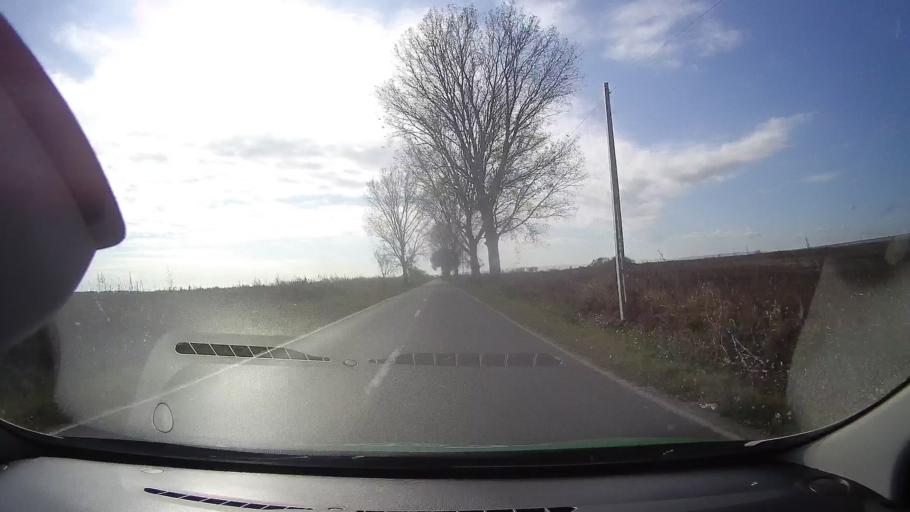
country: RO
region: Tulcea
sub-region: Comuna Valea Nucarilor
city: Agighiol
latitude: 44.9877
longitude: 28.8847
